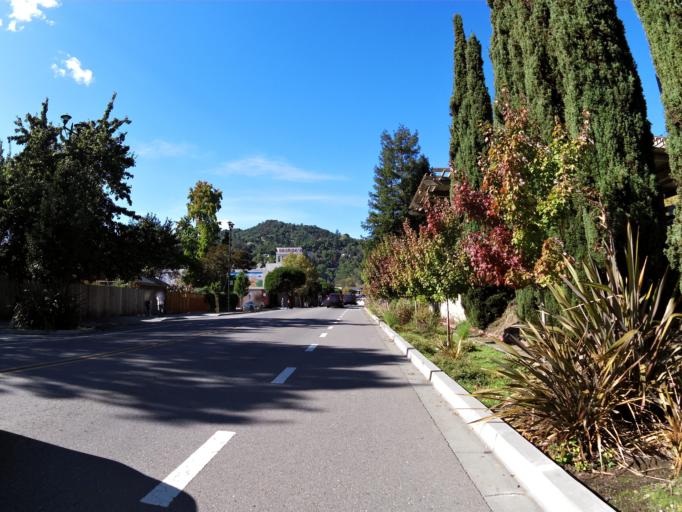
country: US
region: California
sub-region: Marin County
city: Fairfax
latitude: 37.9869
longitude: -122.5863
